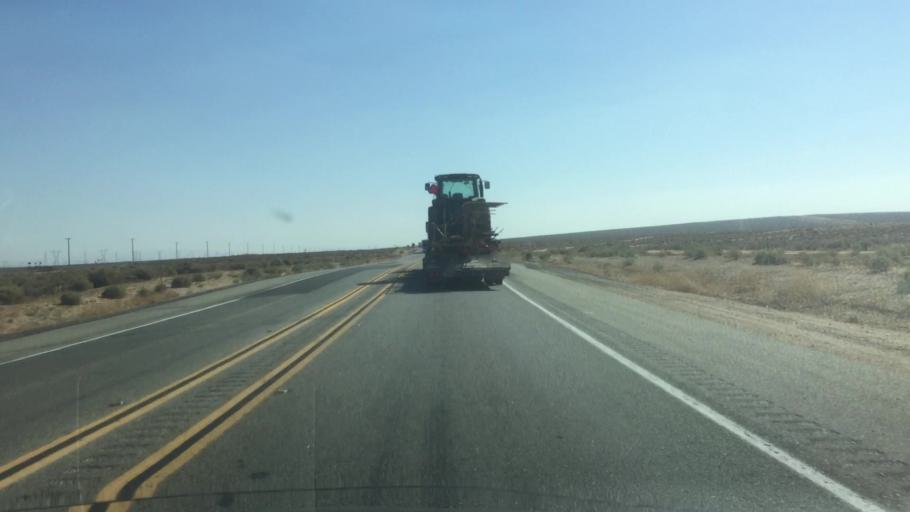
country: US
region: California
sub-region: Kern County
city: Boron
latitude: 34.9911
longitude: -117.5284
